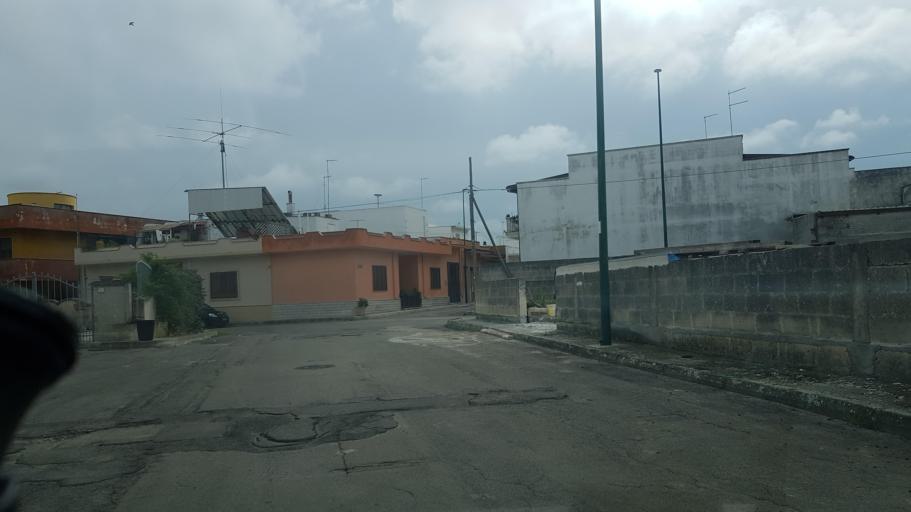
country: IT
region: Apulia
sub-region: Provincia di Lecce
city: Guagnano
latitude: 40.4045
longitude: 17.9452
